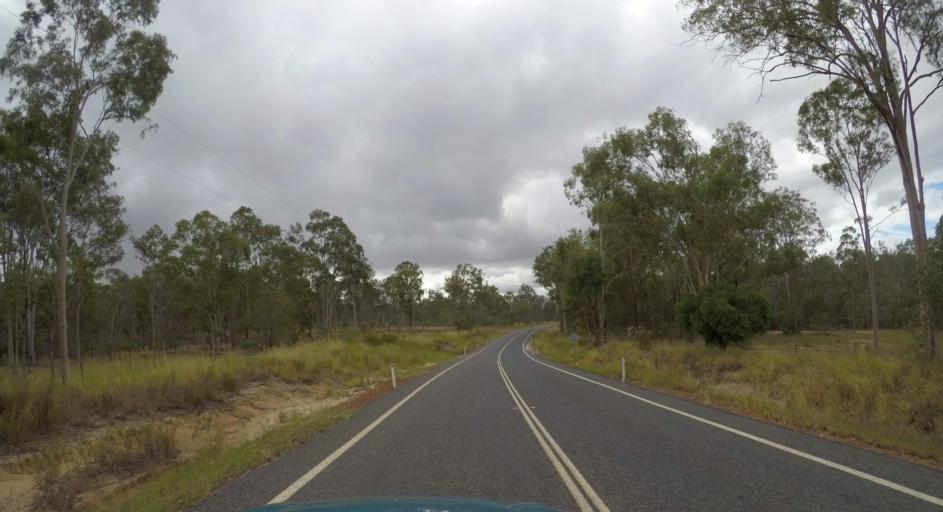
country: AU
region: Queensland
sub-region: North Burnett
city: Gayndah
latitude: -25.3592
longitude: 151.1186
